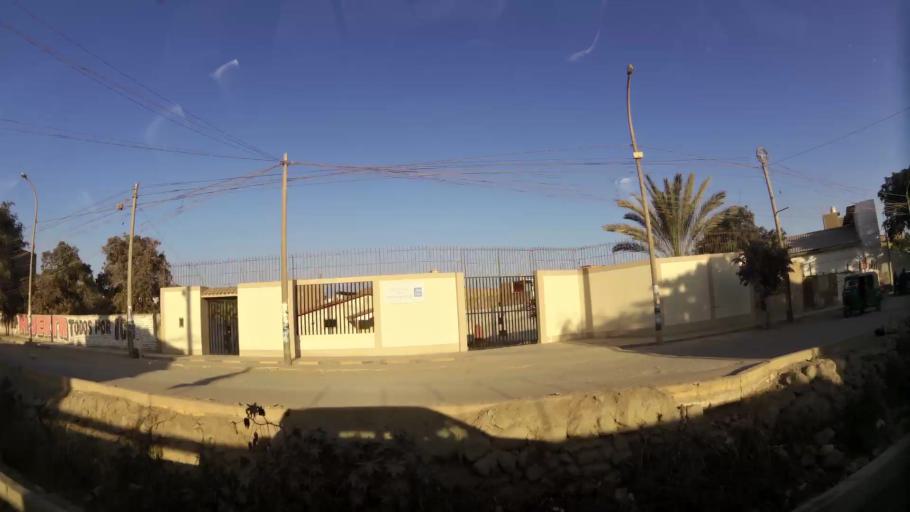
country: PE
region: Ica
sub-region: Provincia de Ica
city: Ica
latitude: -14.0622
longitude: -75.7359
